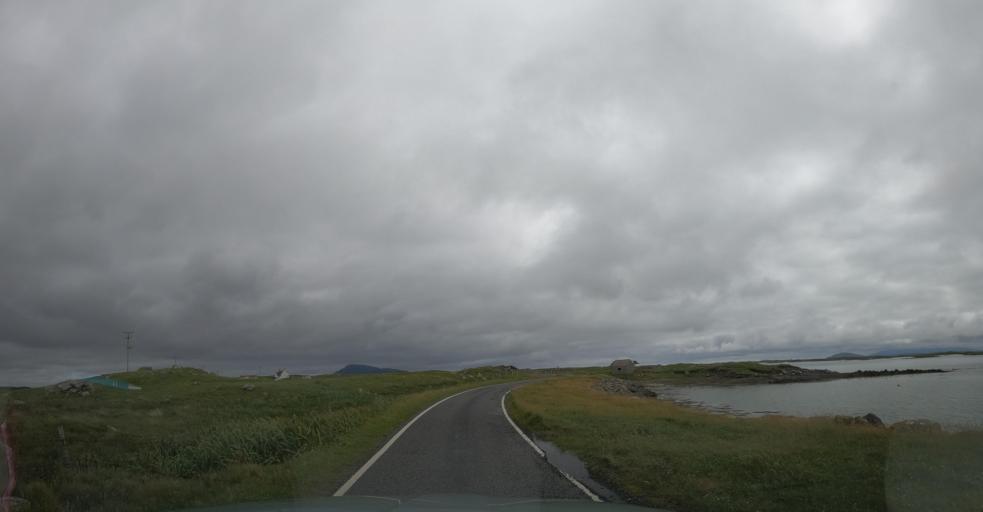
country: GB
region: Scotland
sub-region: Eilean Siar
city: Isle of North Uist
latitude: 57.5418
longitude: -7.3444
